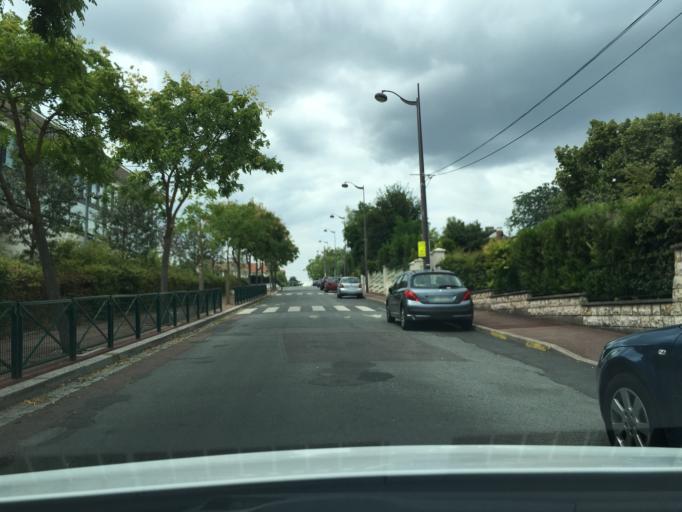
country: FR
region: Ile-de-France
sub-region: Departement des Hauts-de-Seine
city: Rueil-Malmaison
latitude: 48.8672
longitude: 2.1805
